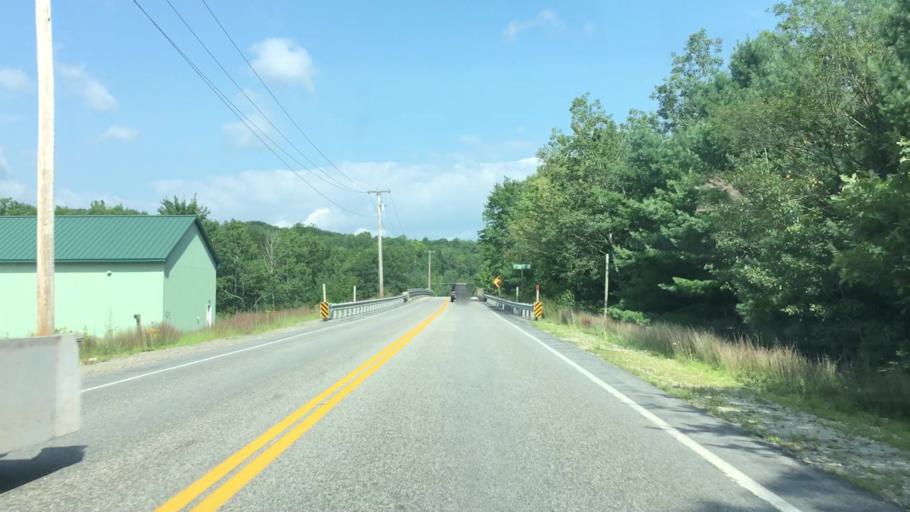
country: US
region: Maine
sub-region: Cumberland County
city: New Gloucester
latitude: 44.0267
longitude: -70.2870
